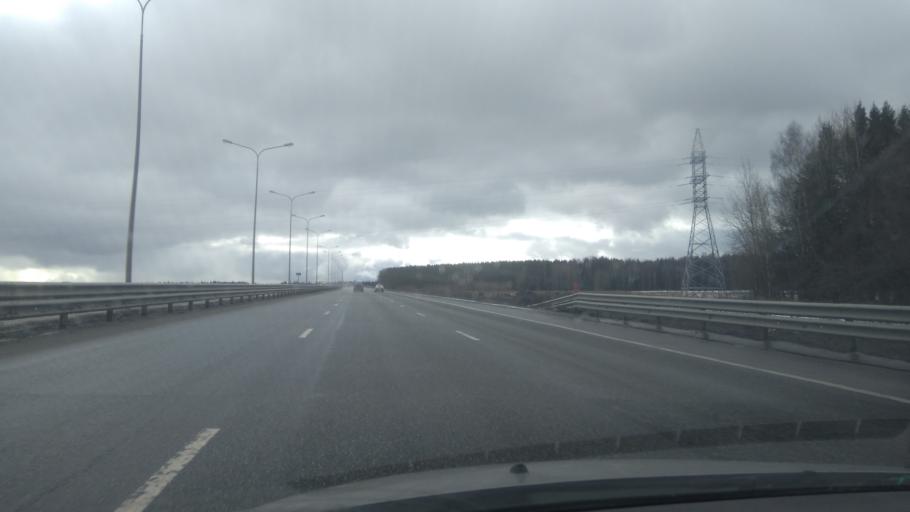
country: RU
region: Perm
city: Bershet'
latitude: 57.7161
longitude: 56.3601
